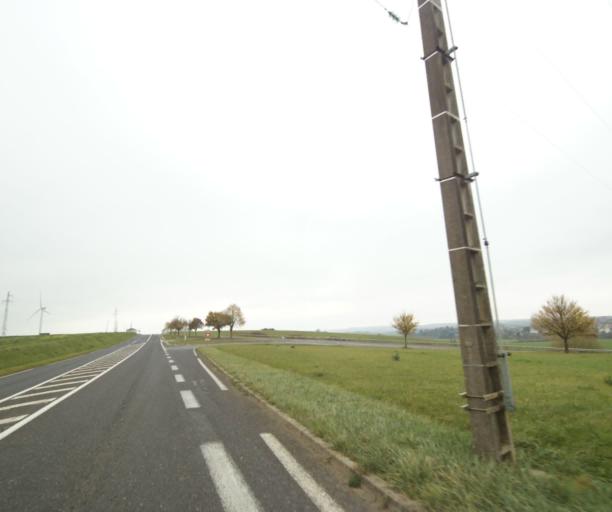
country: FR
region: Lorraine
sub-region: Departement de Meurthe-et-Moselle
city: Mancieulles
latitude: 49.2692
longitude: 5.8979
